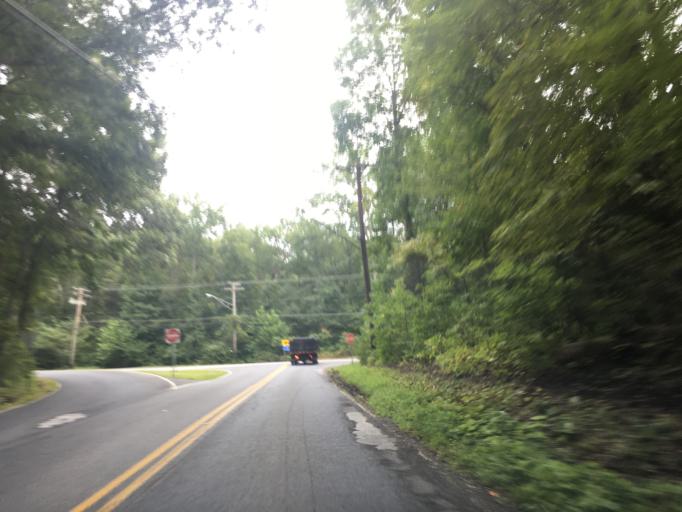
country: US
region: Maryland
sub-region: Anne Arundel County
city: Herald Harbor
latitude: 39.0421
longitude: -76.5816
